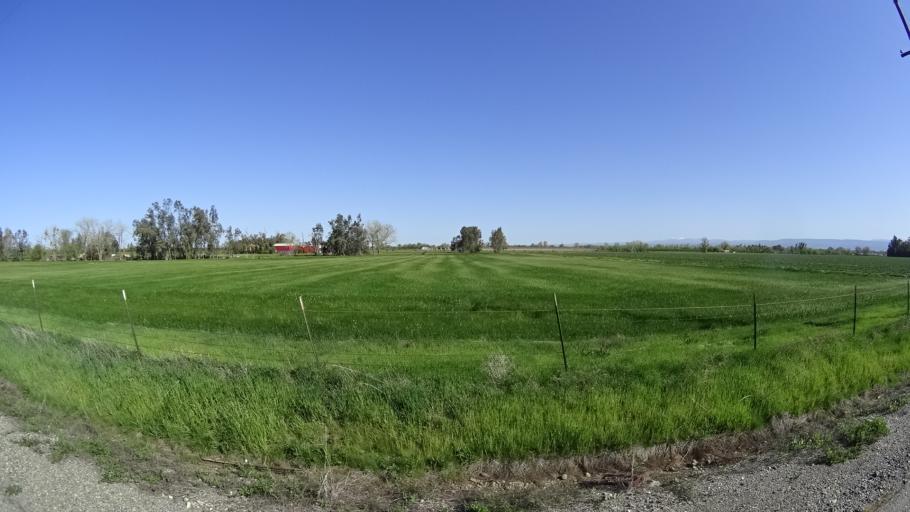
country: US
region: California
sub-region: Glenn County
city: Hamilton City
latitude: 39.7753
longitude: -122.0628
